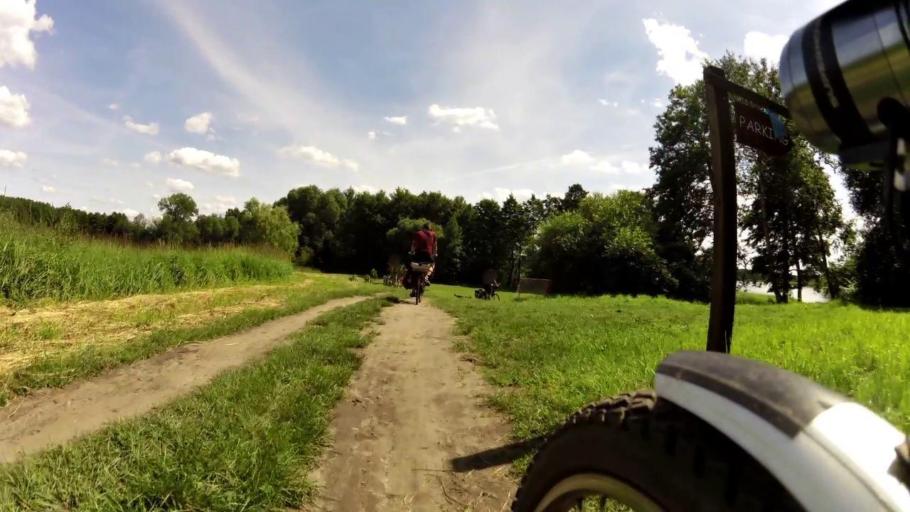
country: PL
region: West Pomeranian Voivodeship
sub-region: Powiat lobeski
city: Radowo Male
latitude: 53.5627
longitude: 15.4155
